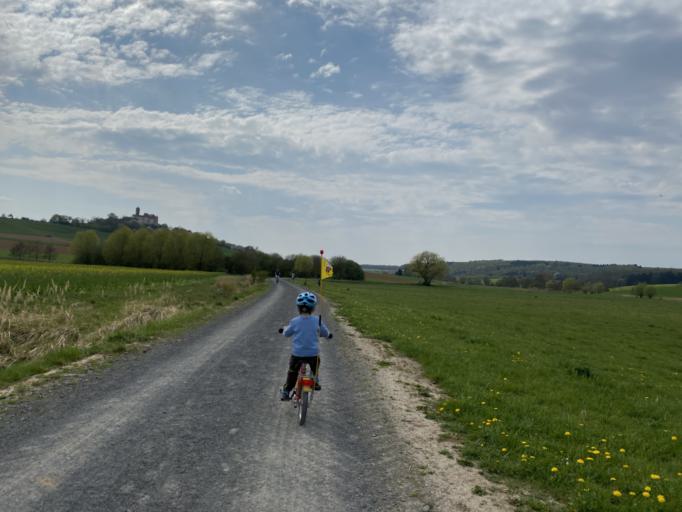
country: DE
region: Hesse
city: Budingen
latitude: 50.2476
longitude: 9.0678
